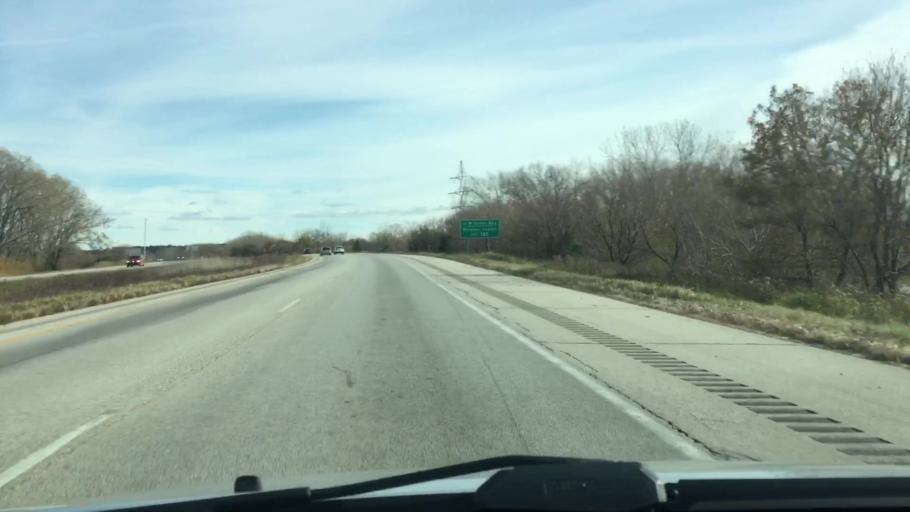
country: US
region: Wisconsin
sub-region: Brown County
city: Green Bay
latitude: 44.5208
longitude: -87.9718
